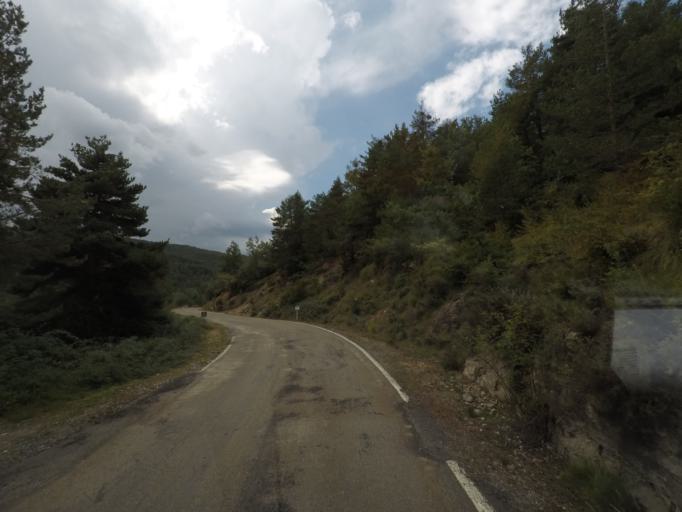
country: ES
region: Aragon
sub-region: Provincia de Huesca
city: Boltana
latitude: 42.3978
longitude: -0.0405
